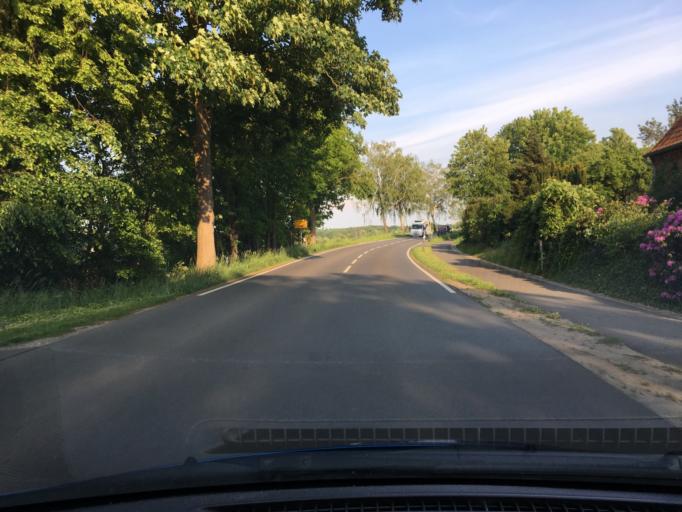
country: DE
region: Lower Saxony
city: Scharnebeck
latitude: 53.2921
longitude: 10.5197
